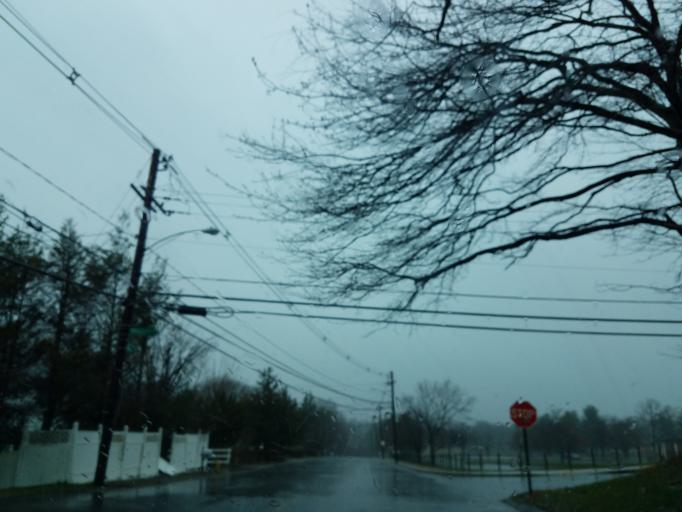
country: US
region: Connecticut
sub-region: New Haven County
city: Waterbury
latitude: 41.5297
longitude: -73.0660
